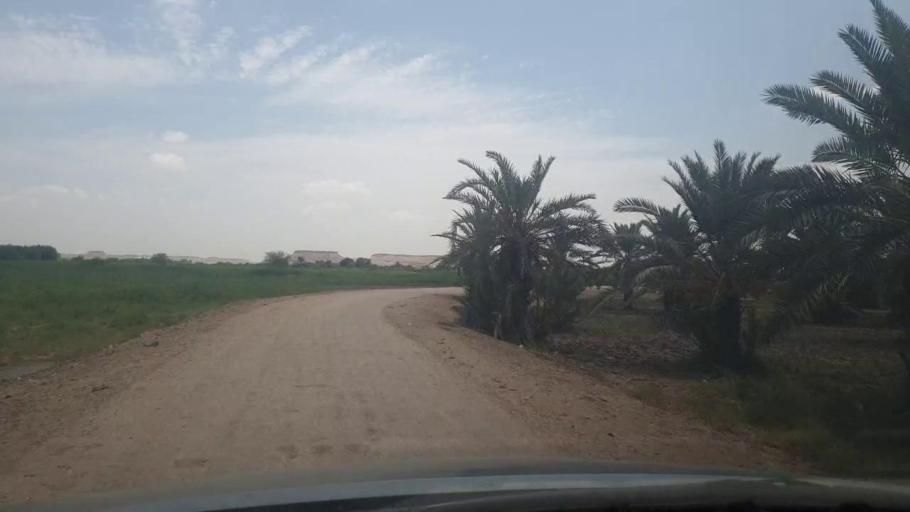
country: PK
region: Sindh
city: Kot Diji
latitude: 27.3941
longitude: 68.7621
